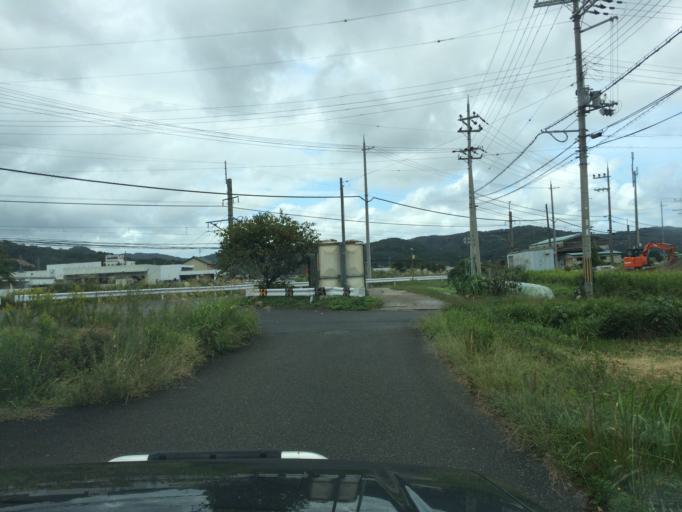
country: JP
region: Hyogo
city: Toyooka
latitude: 35.4798
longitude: 134.7855
